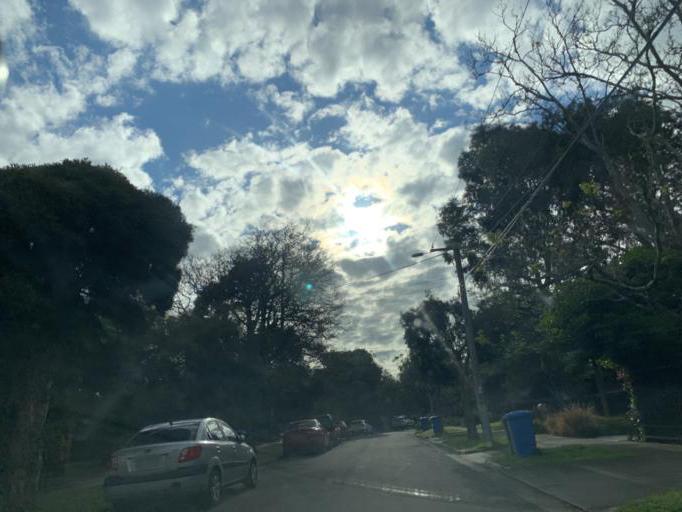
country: AU
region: Victoria
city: Beaumaris
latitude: -37.9803
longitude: 145.0383
